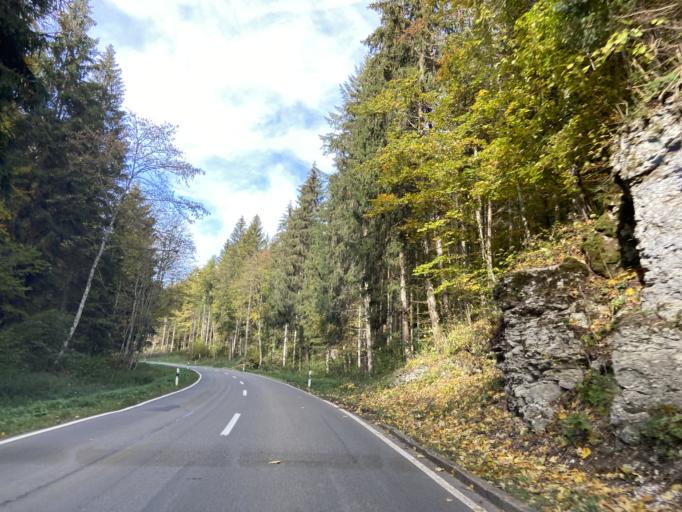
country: DE
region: Baden-Wuerttemberg
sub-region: Tuebingen Region
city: Schwenningen
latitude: 48.0926
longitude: 9.0287
